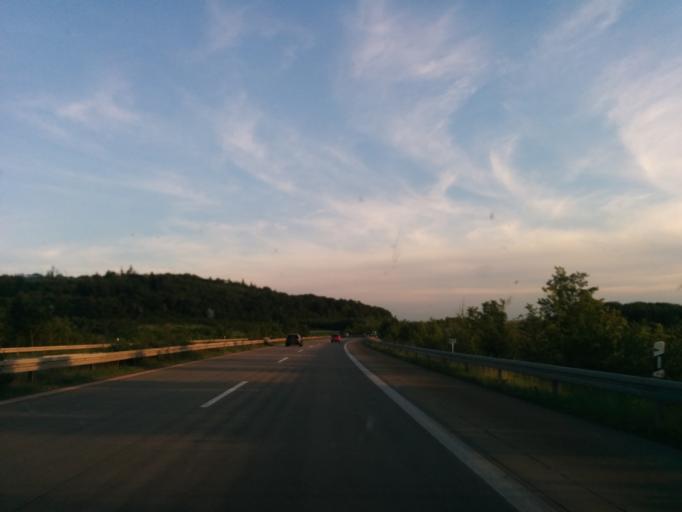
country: DE
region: Bavaria
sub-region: Regierungsbezirk Mittelfranken
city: Gallmersgarten
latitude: 49.4267
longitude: 10.2585
